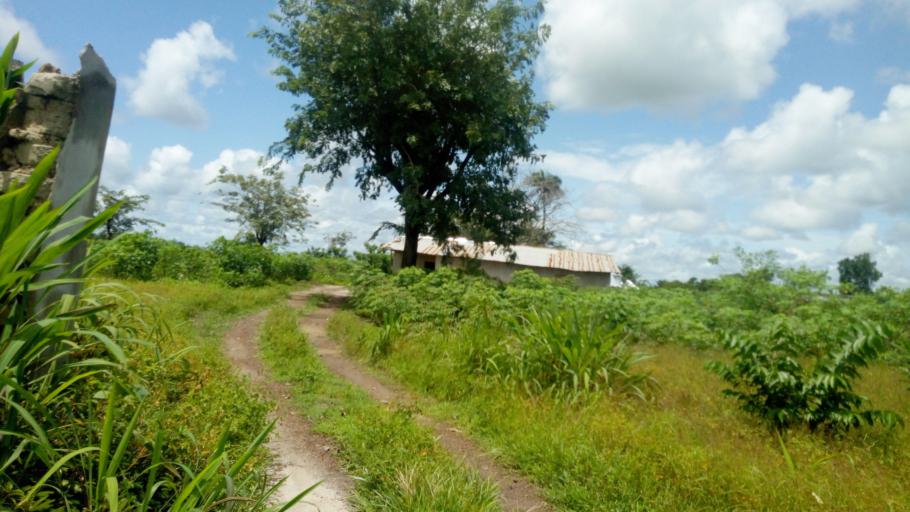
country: SL
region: Northern Province
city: Magburaka
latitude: 8.7117
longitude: -11.9539
